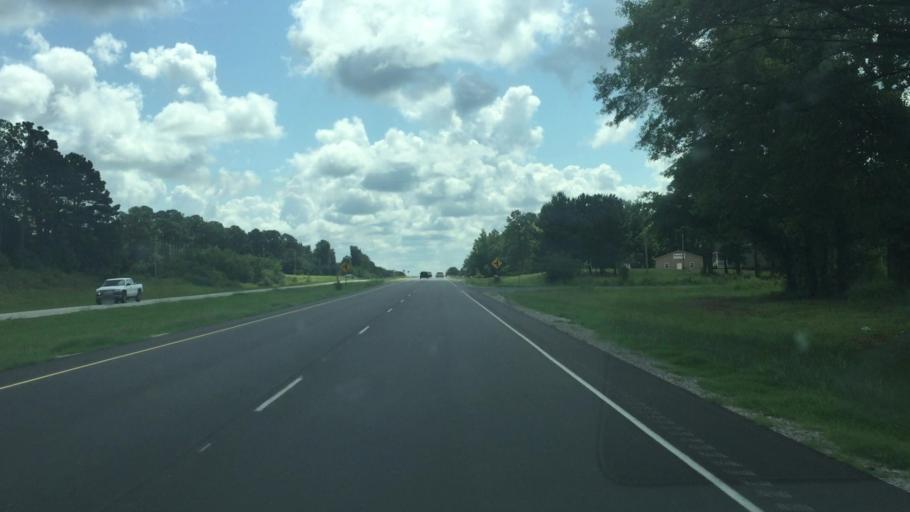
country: US
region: North Carolina
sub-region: Richmond County
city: Cordova
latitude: 34.9488
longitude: -79.9041
